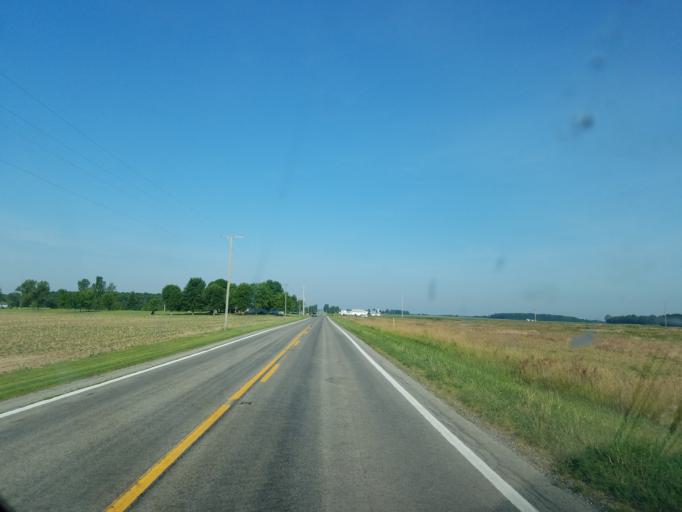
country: US
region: Ohio
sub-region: Hardin County
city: Kenton
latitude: 40.7320
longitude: -83.6488
